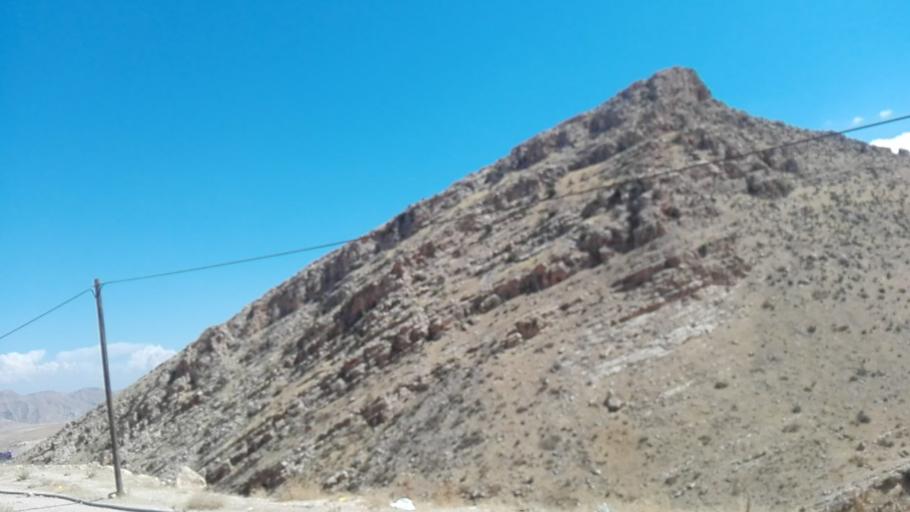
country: TR
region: Batman
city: Hasankeyf
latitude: 37.6994
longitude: 41.4588
